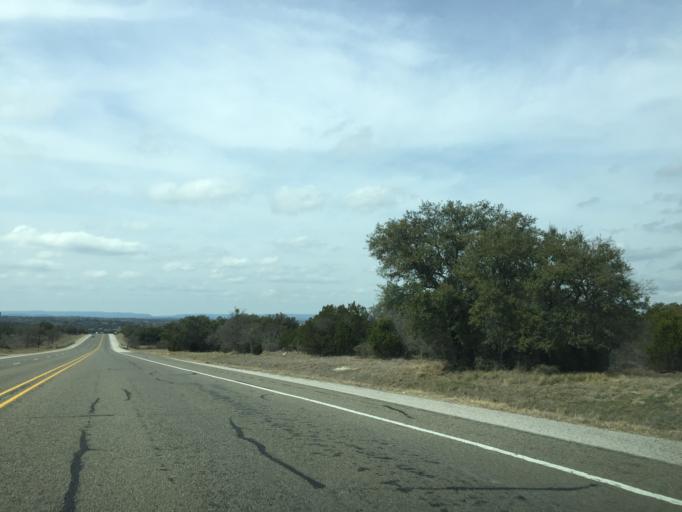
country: US
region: Texas
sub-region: Llano County
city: Horseshoe Bay
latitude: 30.5138
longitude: -98.3863
